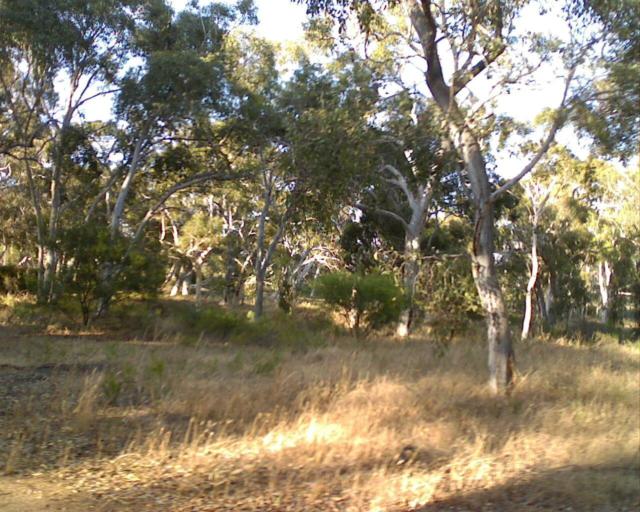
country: AU
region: Western Australia
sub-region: Dandaragan
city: Jurien Bay
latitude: -30.0632
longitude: 115.1786
